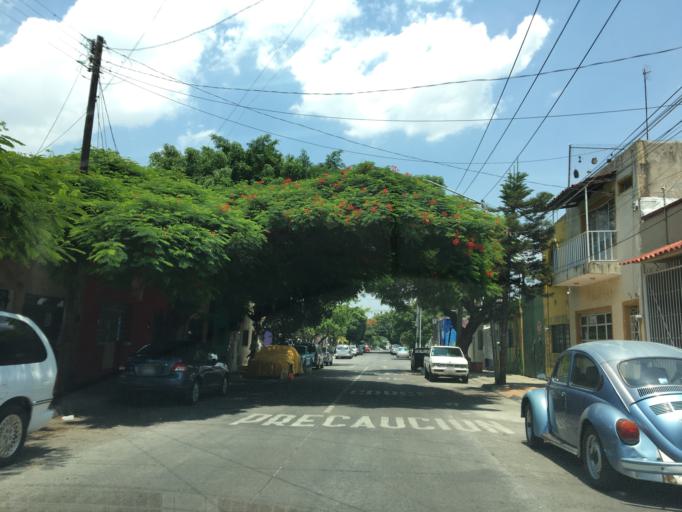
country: MX
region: Jalisco
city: Guadalajara
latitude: 20.6582
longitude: -103.3669
